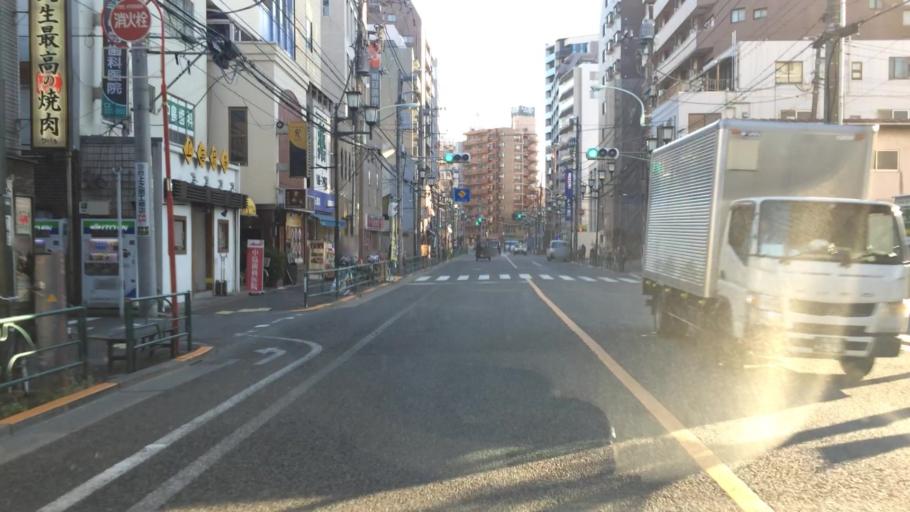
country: JP
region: Tokyo
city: Tokyo
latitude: 35.7231
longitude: 139.7625
